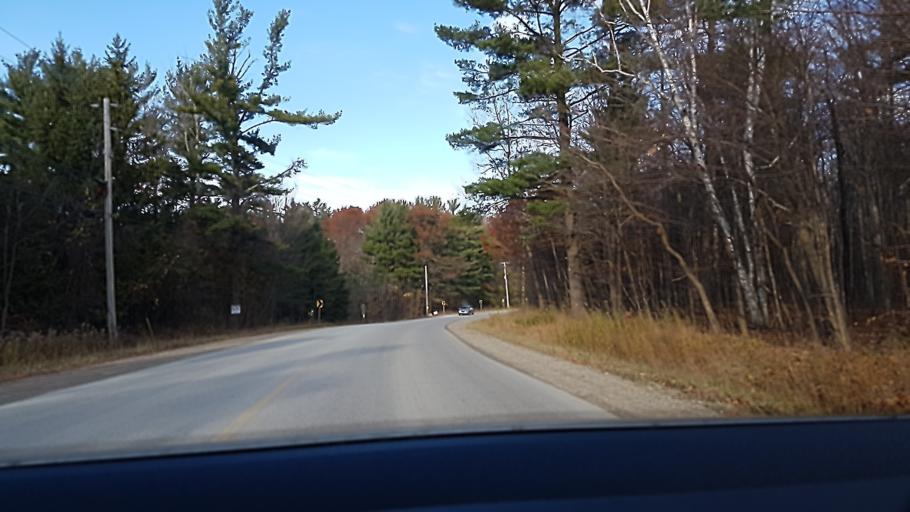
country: CA
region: Ontario
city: Barrie
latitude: 44.3903
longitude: -79.5529
